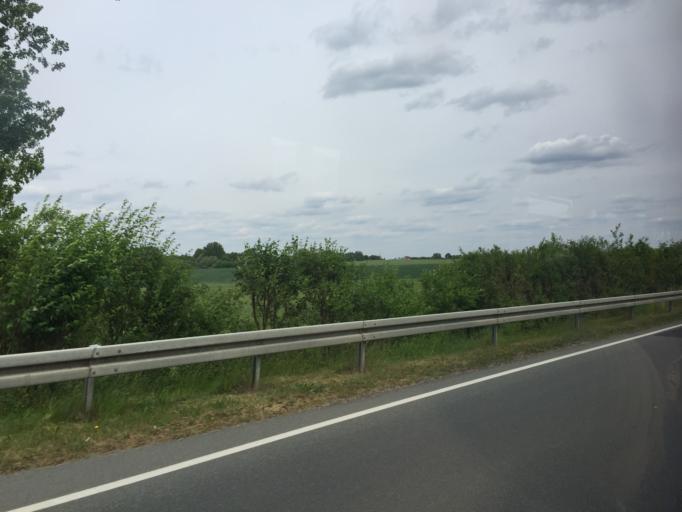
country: DE
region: Saxony
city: Goerlitz
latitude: 51.1541
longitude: 14.9424
